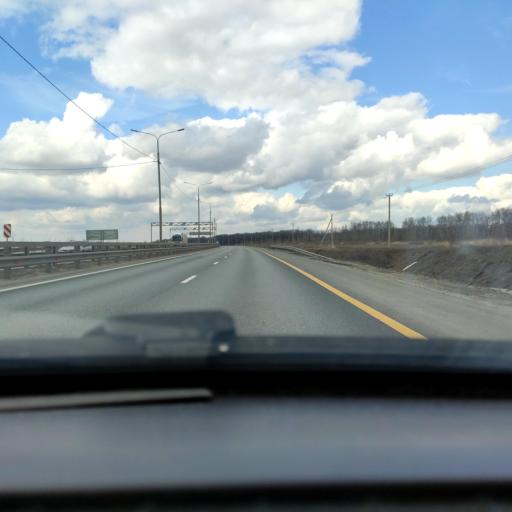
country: RU
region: Tula
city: Yefremov
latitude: 52.9685
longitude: 38.2325
